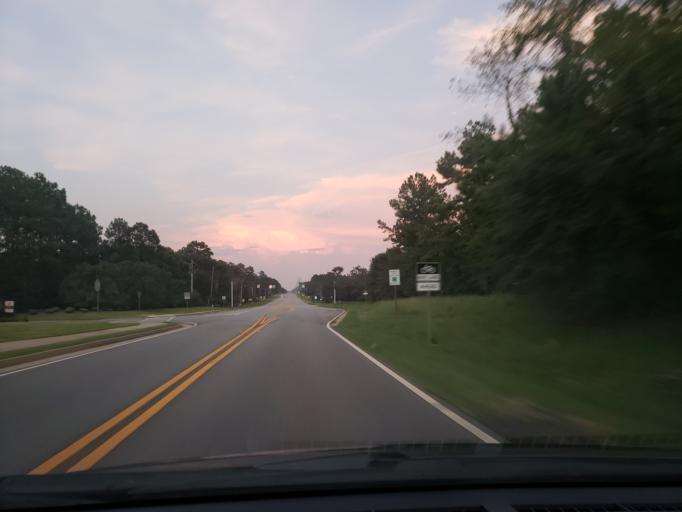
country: US
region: Georgia
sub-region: Dougherty County
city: Albany
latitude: 31.5857
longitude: -84.2892
